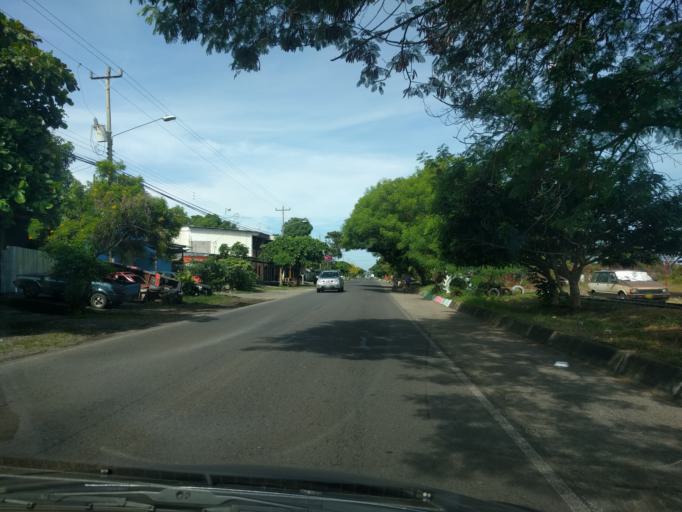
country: CR
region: Puntarenas
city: Esparza
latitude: 9.9864
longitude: -84.7163
